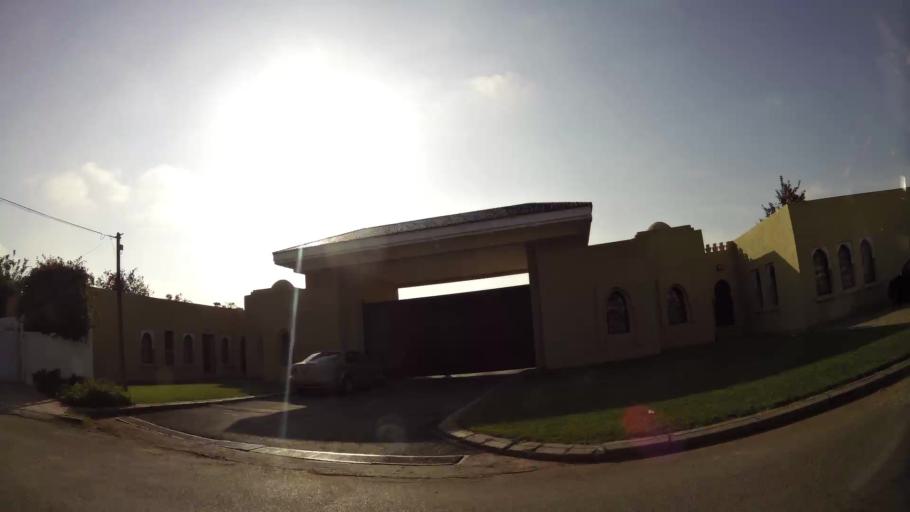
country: MA
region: Rabat-Sale-Zemmour-Zaer
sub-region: Rabat
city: Rabat
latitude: 33.9370
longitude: -6.8151
